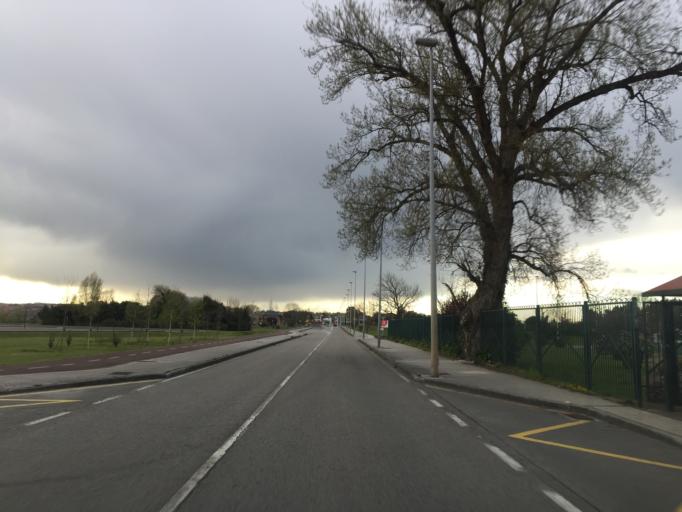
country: ES
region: Asturias
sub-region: Province of Asturias
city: Gijon
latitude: 43.5248
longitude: -5.6239
